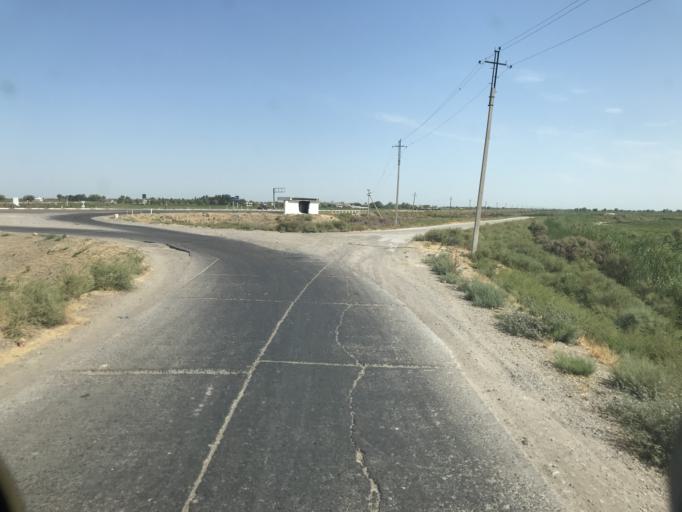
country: KZ
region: Ongtustik Qazaqstan
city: Myrzakent
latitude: 40.7481
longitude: 68.5377
